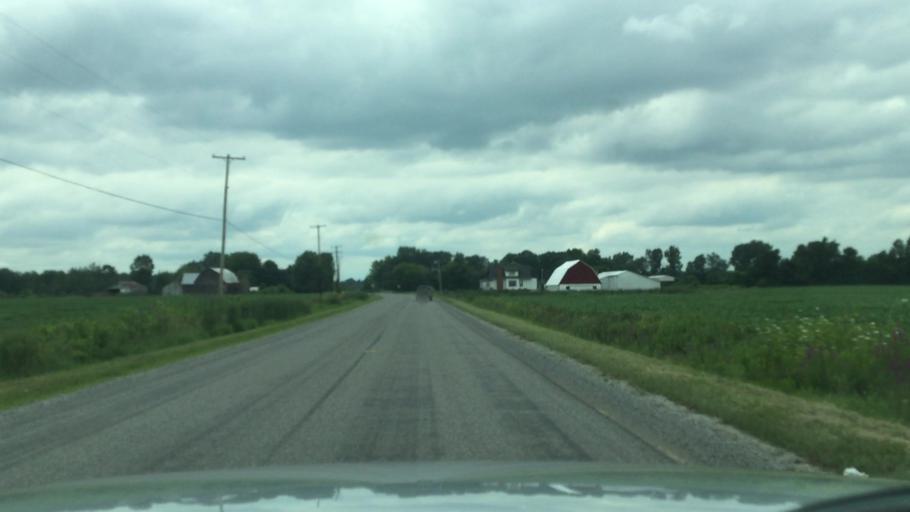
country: US
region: Michigan
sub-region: Saginaw County
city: Birch Run
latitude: 43.2508
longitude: -83.8420
